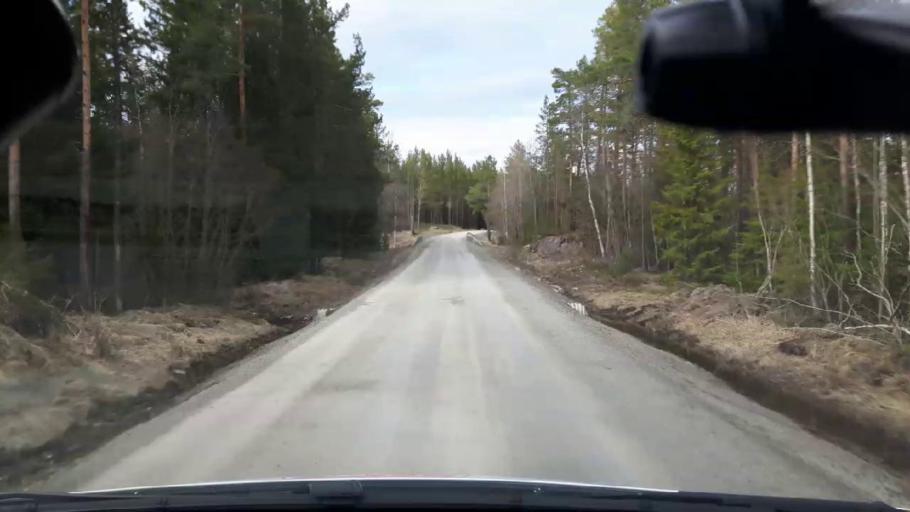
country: SE
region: Jaemtland
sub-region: OEstersunds Kommun
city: Brunflo
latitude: 62.9322
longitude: 14.6498
